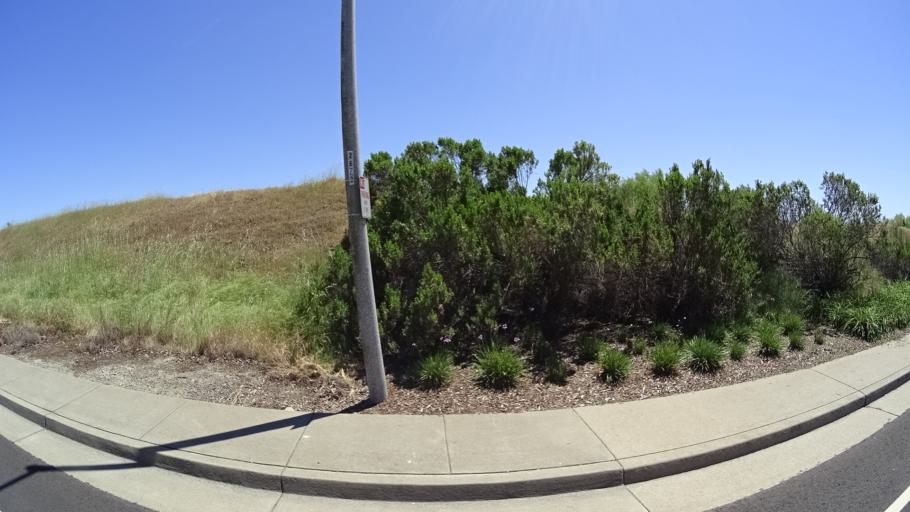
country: US
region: California
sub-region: Placer County
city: Rocklin
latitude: 38.8132
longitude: -121.2788
